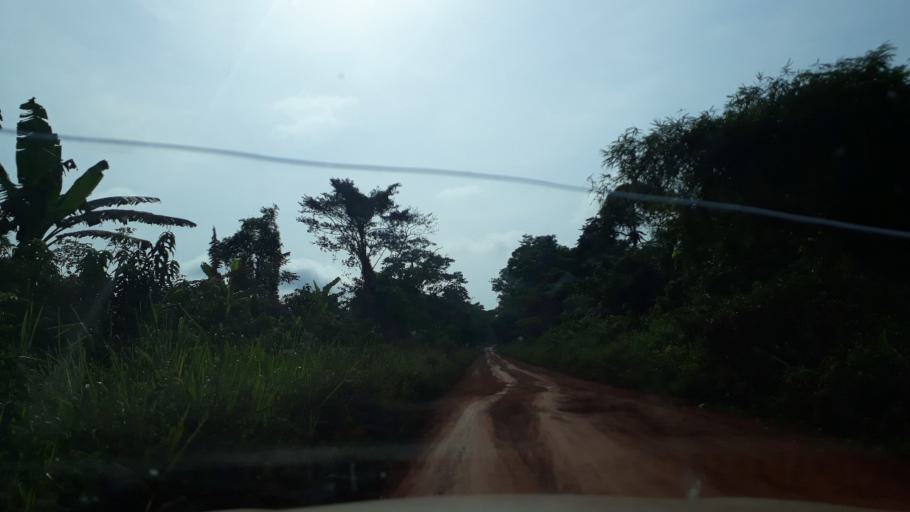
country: CD
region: Eastern Province
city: Wamba
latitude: 1.4051
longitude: 27.6519
